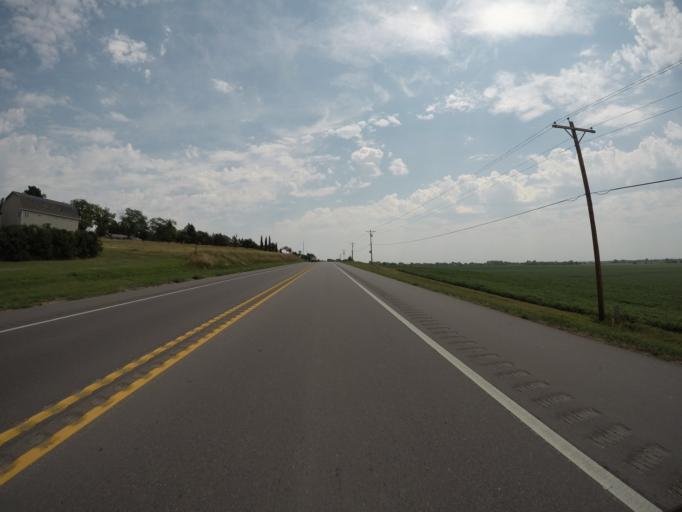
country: US
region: Nebraska
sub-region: Buffalo County
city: Kearney
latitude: 40.6994
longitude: -99.1560
